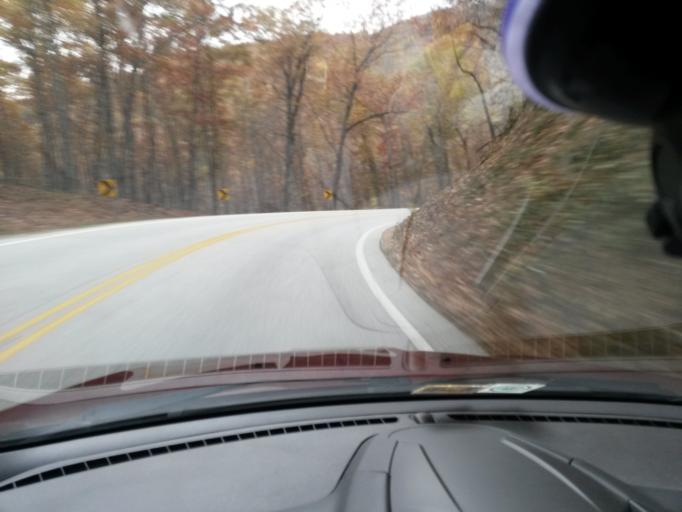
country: US
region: Virginia
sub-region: Rockbridge County
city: Glasgow
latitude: 37.6137
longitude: -79.4180
